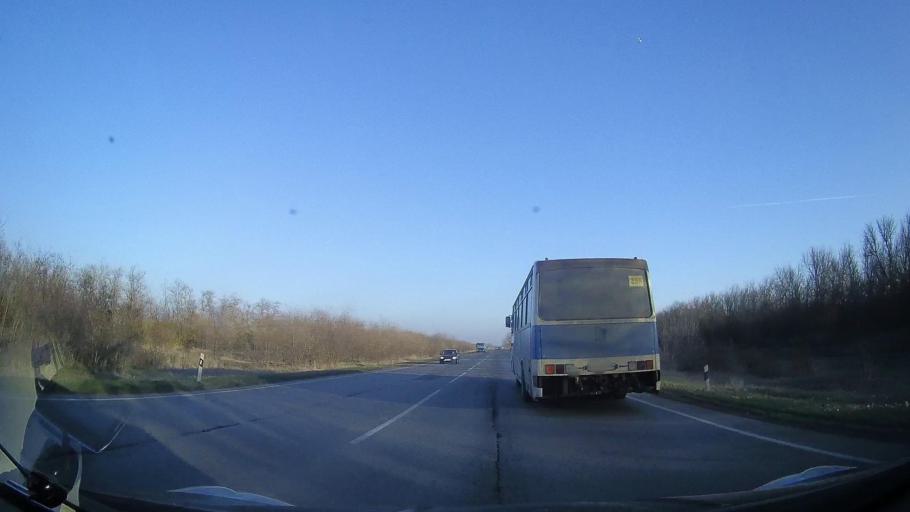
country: RU
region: Rostov
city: Kirovskaya
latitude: 47.0160
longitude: 39.9108
